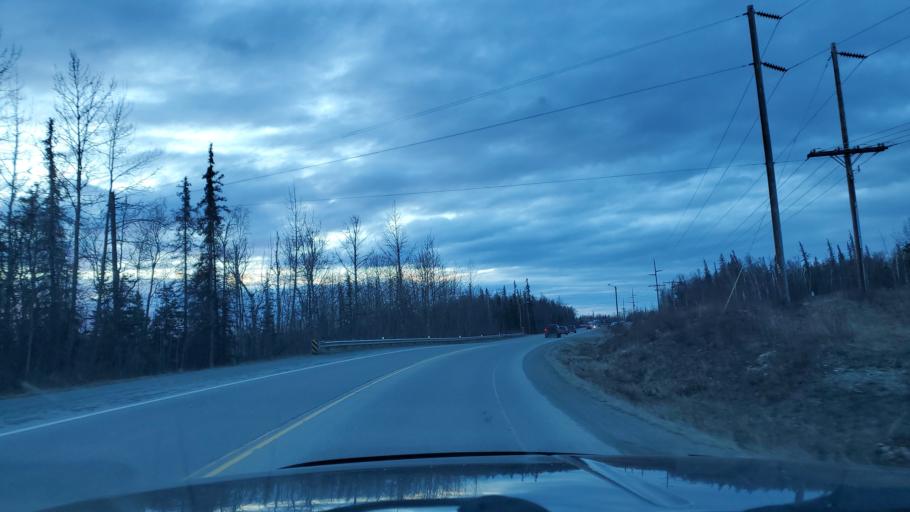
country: US
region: Alaska
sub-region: Matanuska-Susitna Borough
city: Tanaina
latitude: 61.5941
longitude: -149.3794
